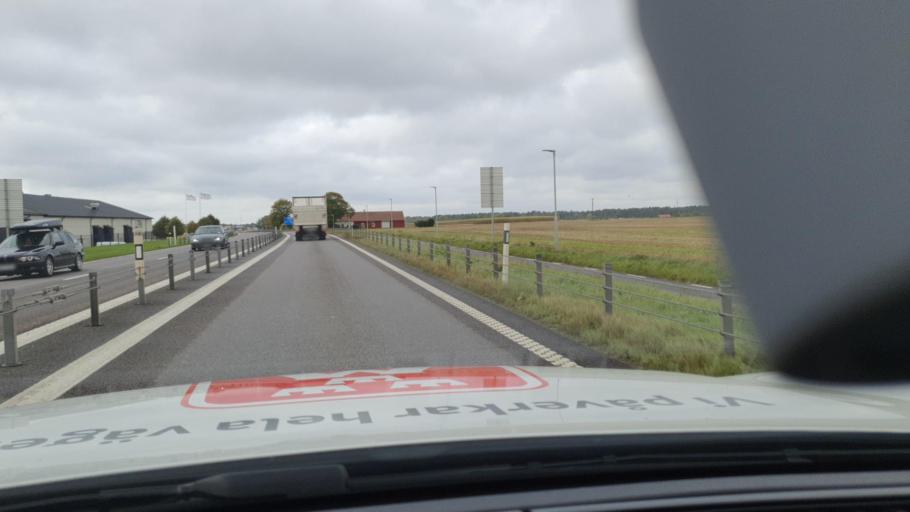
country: SE
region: Halland
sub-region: Laholms Kommun
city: Laholm
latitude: 56.5037
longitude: 12.9887
